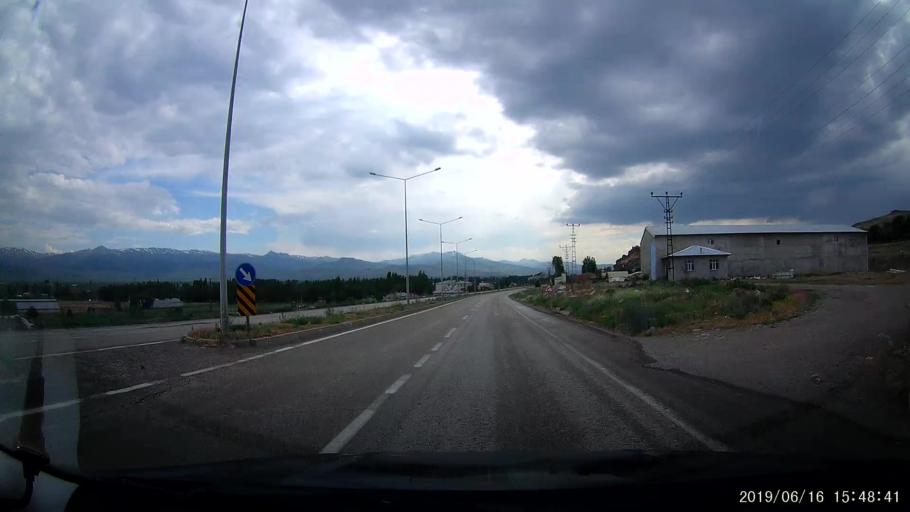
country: TR
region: Erzurum
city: Pasinler
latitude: 39.9811
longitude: 41.6970
